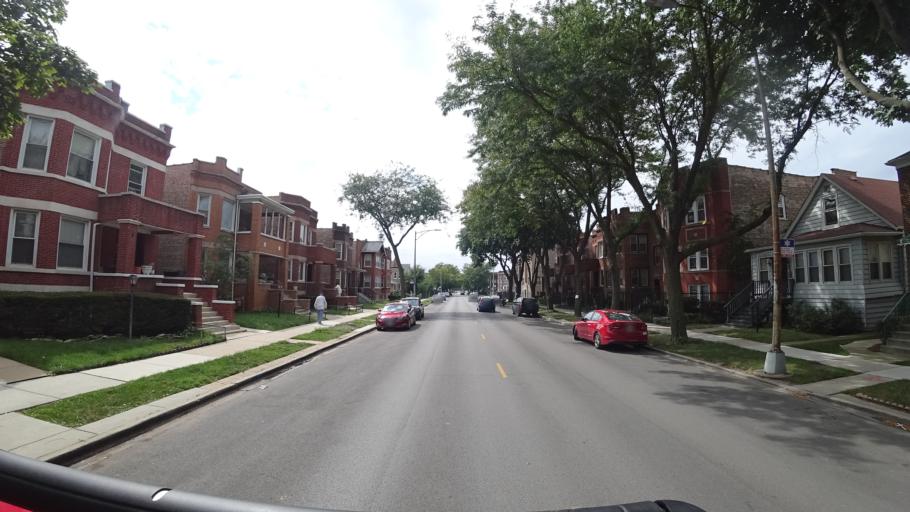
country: US
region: Illinois
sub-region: Cook County
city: Oak Park
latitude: 41.8766
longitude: -87.7586
